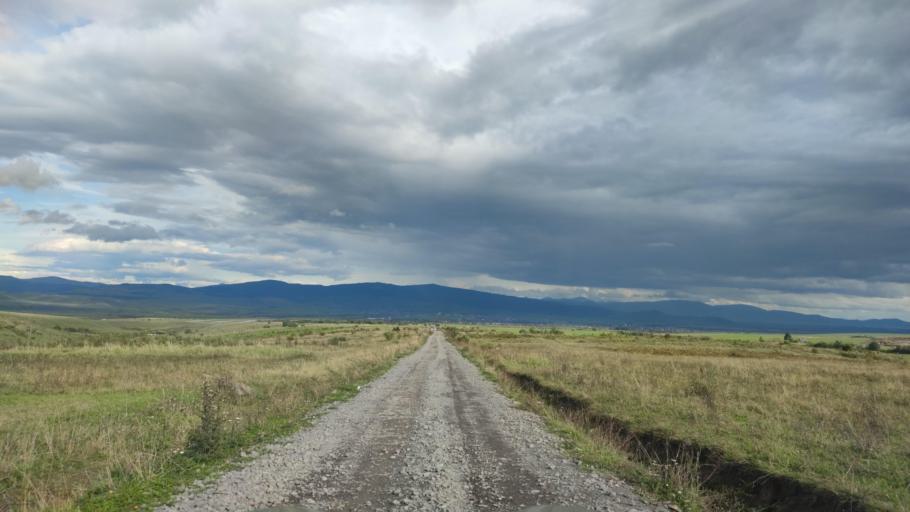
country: RO
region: Harghita
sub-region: Comuna Remetea
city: Remetea
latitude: 46.8162
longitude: 25.3719
